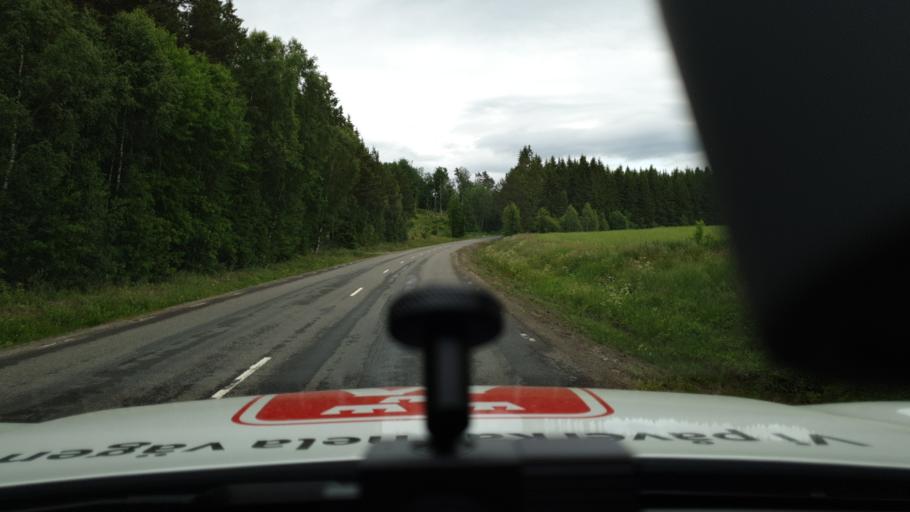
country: SE
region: Joenkoeping
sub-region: Mullsjo Kommun
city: Mullsjoe
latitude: 57.9870
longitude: 13.7919
